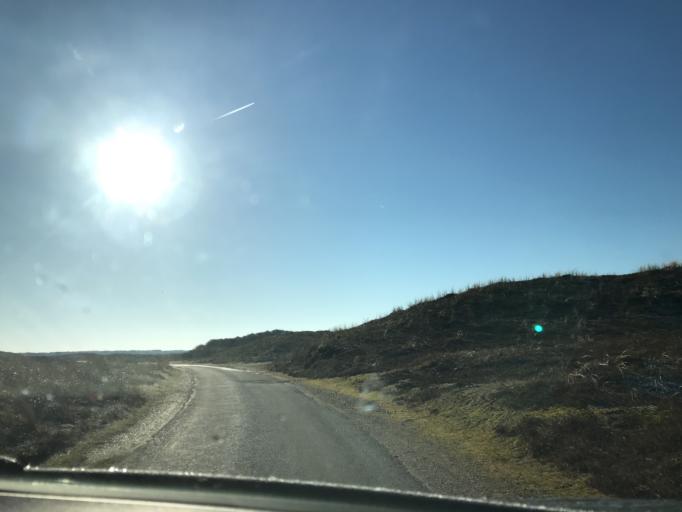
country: DK
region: Central Jutland
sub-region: Ringkobing-Skjern Kommune
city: Hvide Sande
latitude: 55.8139
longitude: 8.1763
